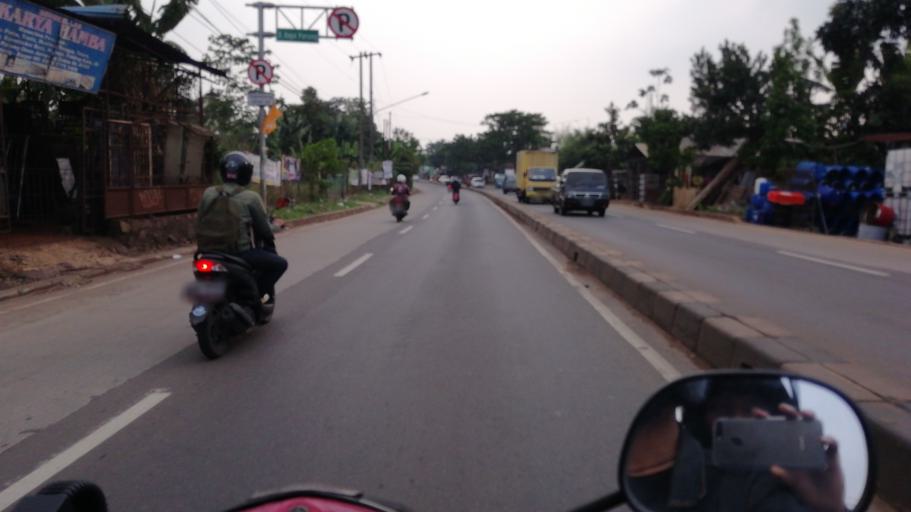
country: ID
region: West Java
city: Parung
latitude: -6.4648
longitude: 106.7294
